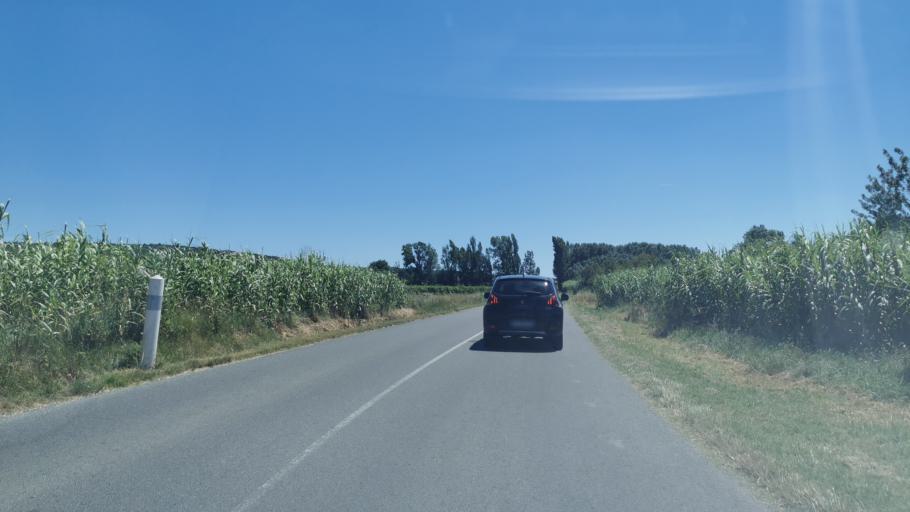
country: FR
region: Languedoc-Roussillon
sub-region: Departement de l'Aude
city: Vinassan
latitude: 43.2174
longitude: 3.0795
